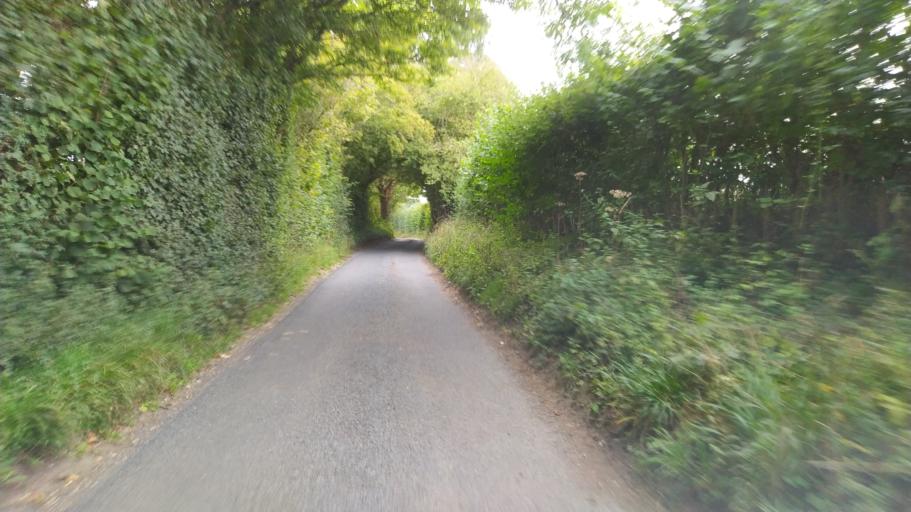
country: GB
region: England
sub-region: Hampshire
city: Long Sutton
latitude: 51.2021
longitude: -0.8933
